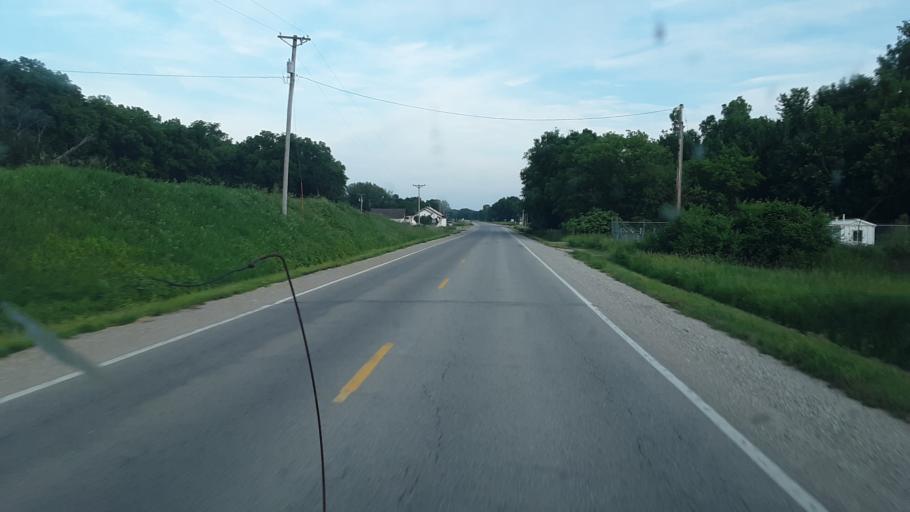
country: US
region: Iowa
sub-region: Benton County
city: Belle Plaine
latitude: 41.9296
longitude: -92.3964
